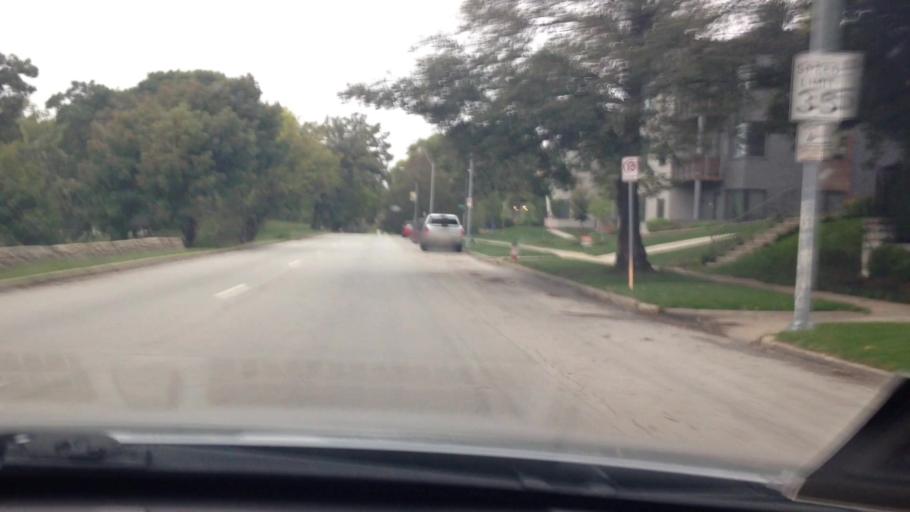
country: US
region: Missouri
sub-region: Jackson County
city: Kansas City
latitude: 39.0612
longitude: -94.5823
